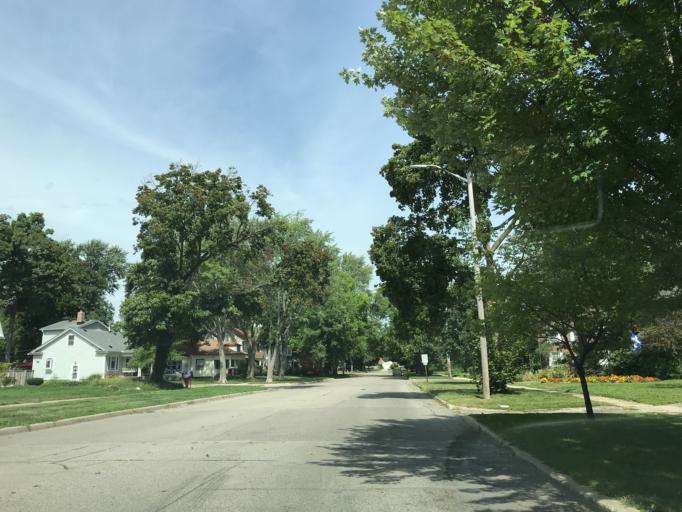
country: US
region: Michigan
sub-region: Washtenaw County
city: Ypsilanti
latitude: 42.2430
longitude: -83.6325
